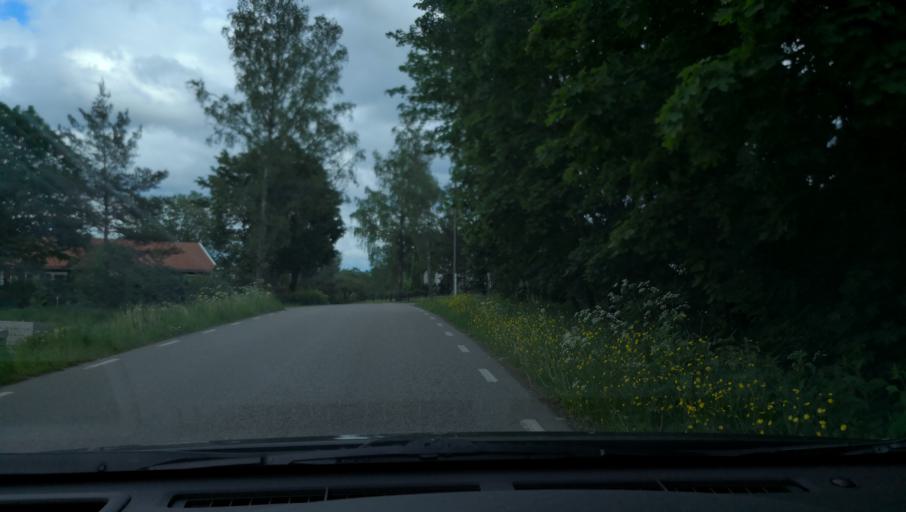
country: SE
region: OErebro
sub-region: Lindesbergs Kommun
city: Fellingsbro
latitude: 59.3273
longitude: 15.6748
